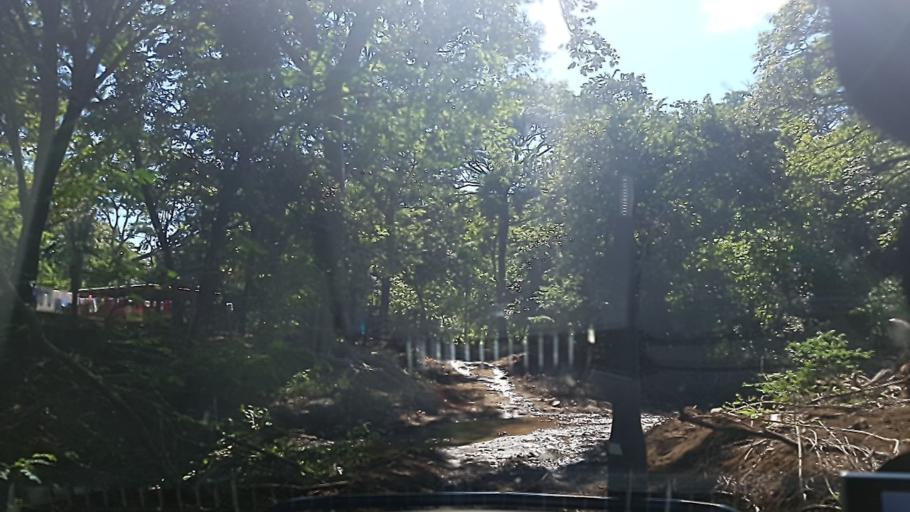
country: NI
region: Rivas
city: Tola
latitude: 11.5640
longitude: -86.0872
